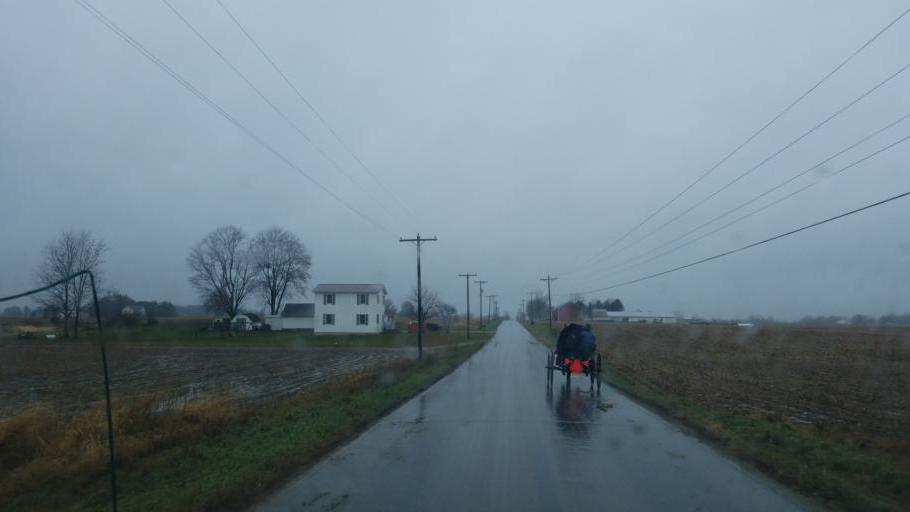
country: US
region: Indiana
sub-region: Adams County
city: Berne
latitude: 40.6435
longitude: -84.9390
